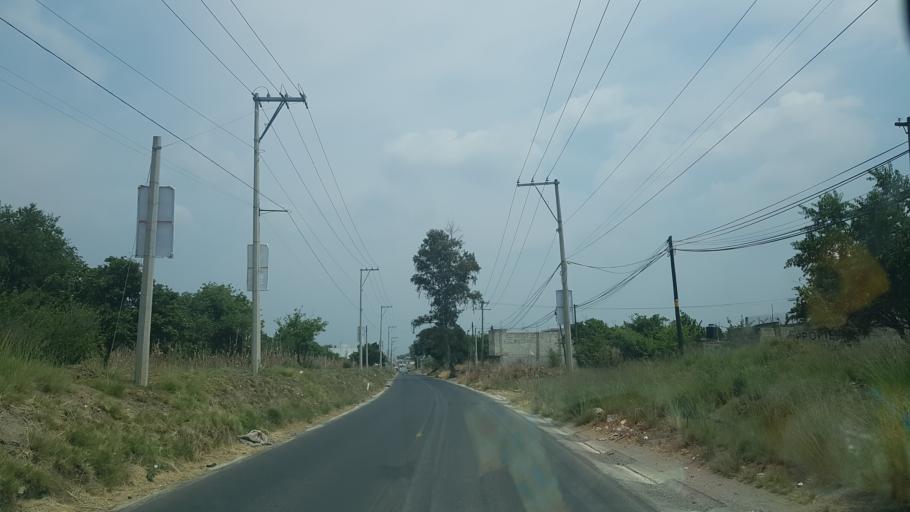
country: MX
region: Puebla
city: Huejotzingo
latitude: 19.1459
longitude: -98.4099
